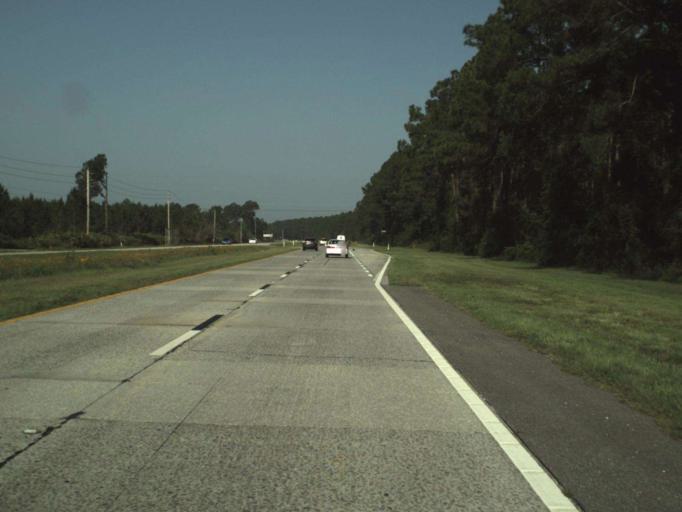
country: US
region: Florida
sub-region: Volusia County
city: Samsula-Spruce Creek
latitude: 29.1343
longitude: -81.1473
